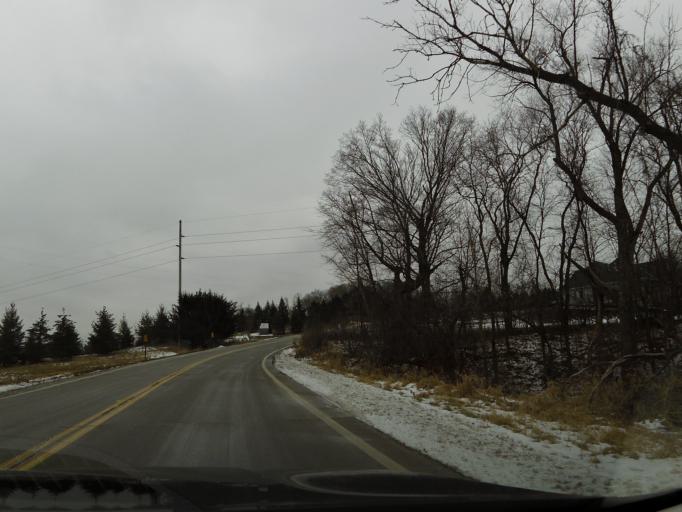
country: US
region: Minnesota
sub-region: Hennepin County
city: Orono
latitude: 45.0008
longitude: -93.5996
